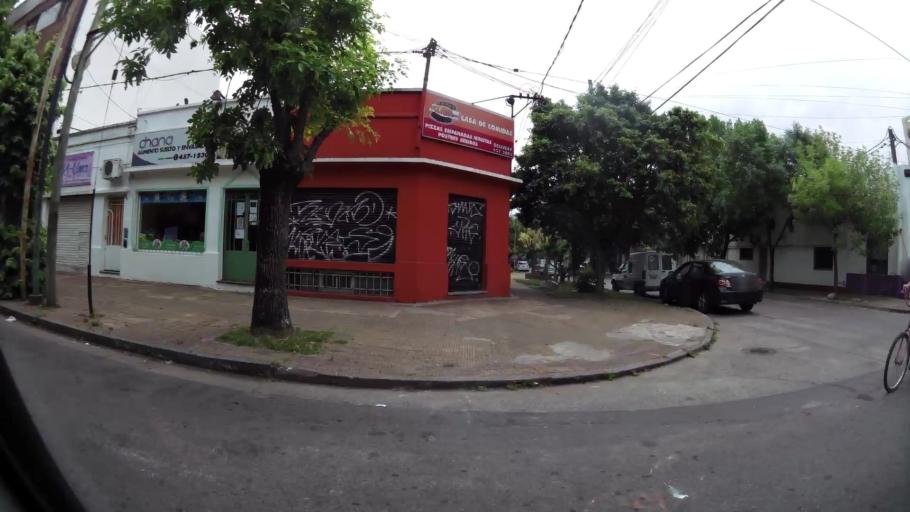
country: AR
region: Buenos Aires
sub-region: Partido de La Plata
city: La Plata
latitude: -34.9425
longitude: -57.9653
